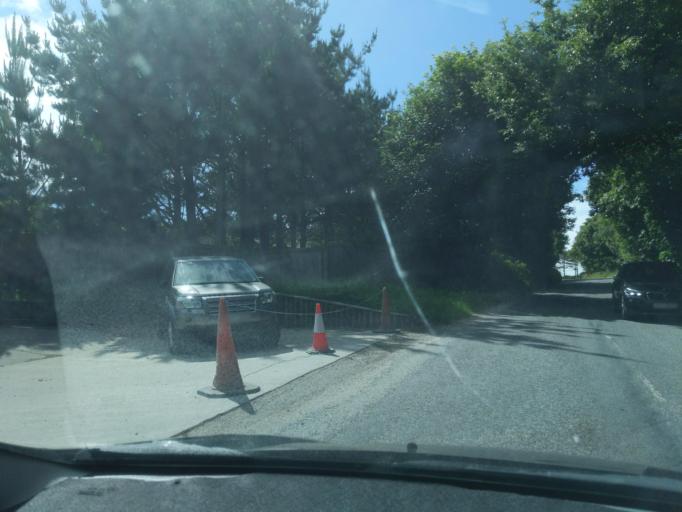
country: GB
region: England
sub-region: Cornwall
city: Perranporth
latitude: 50.2979
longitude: -5.1423
